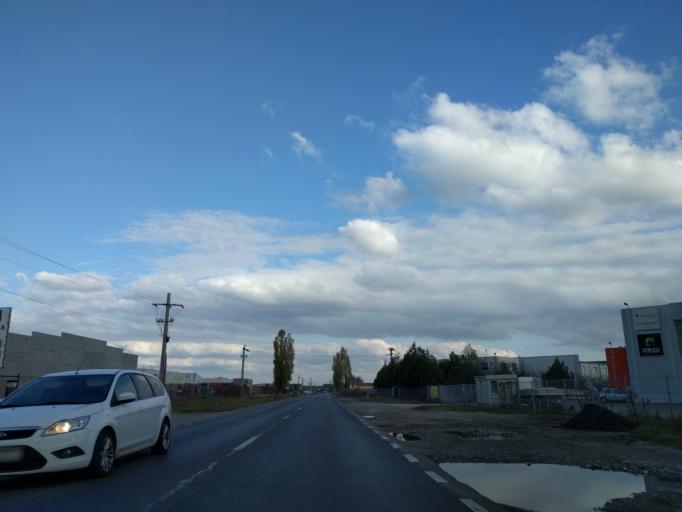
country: RO
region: Ilfov
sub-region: Comuna Ganeasa
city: Ganeasa
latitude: 44.4539
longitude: 26.2652
